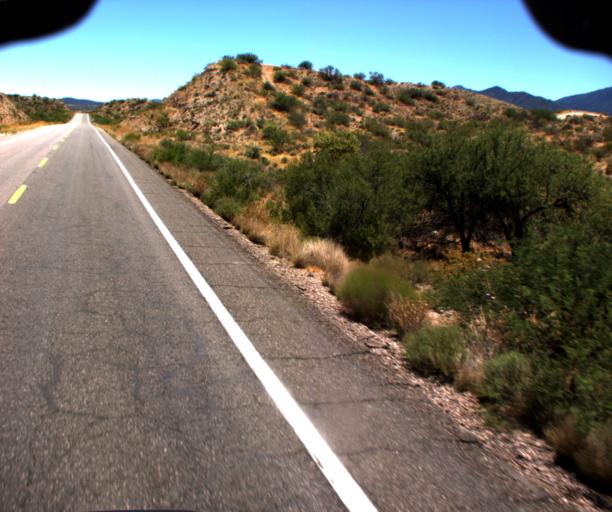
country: US
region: Arizona
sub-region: Gila County
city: Globe
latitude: 33.3690
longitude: -110.7375
